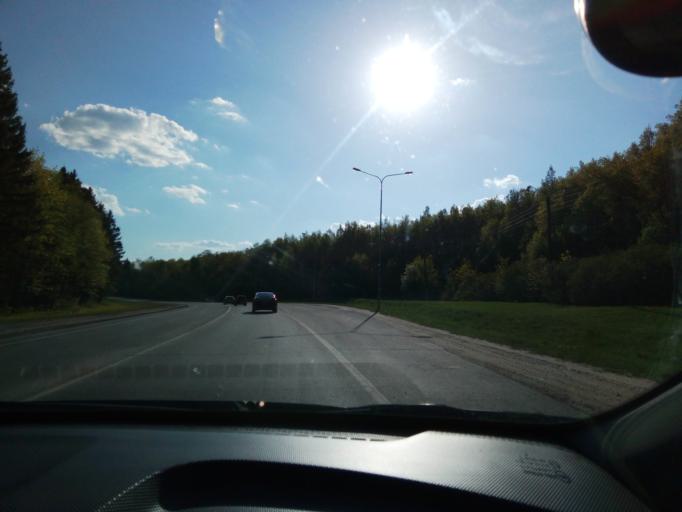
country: RU
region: Chuvashia
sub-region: Cheboksarskiy Rayon
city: Cheboksary
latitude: 56.1352
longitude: 47.1745
